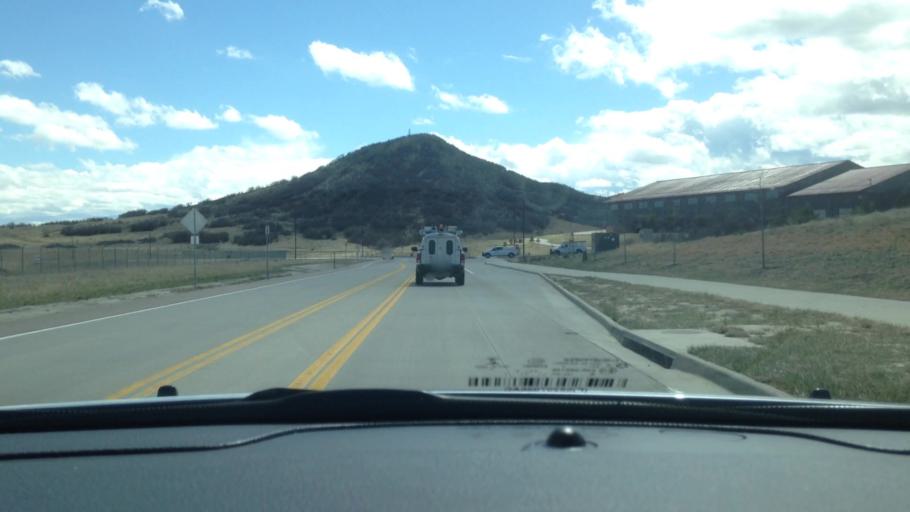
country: US
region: Colorado
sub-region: Douglas County
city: Castle Rock
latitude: 39.3724
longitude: -104.8774
